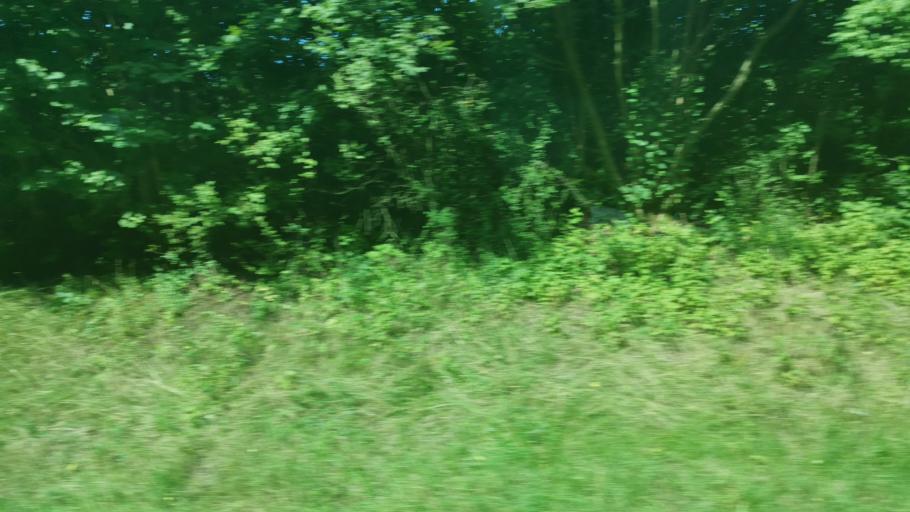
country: DE
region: Bavaria
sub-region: Upper Palatinate
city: Pemfling
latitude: 49.2900
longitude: 12.6272
